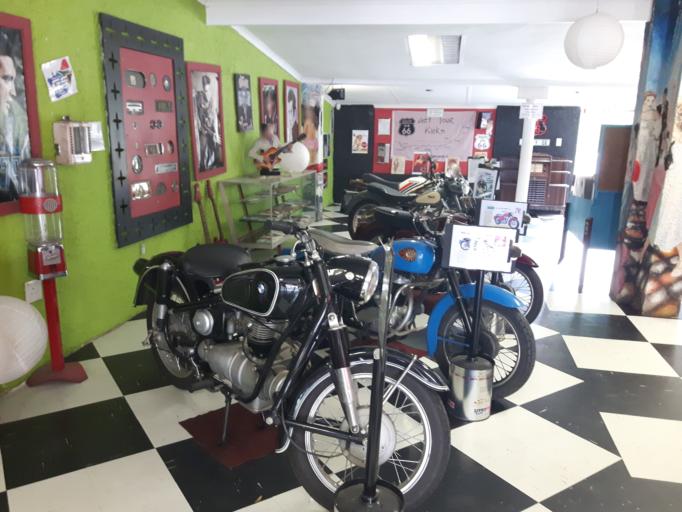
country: ZA
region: Eastern Cape
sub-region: Cacadu District Municipality
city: Kareedouw
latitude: -33.9742
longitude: 23.8873
